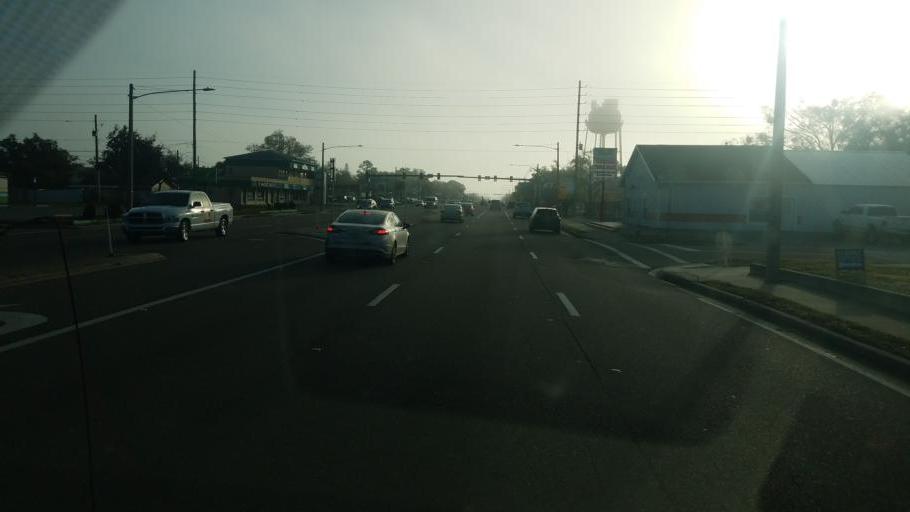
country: US
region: Florida
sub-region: Osceola County
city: Saint Cloud
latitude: 28.2459
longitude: -81.2884
